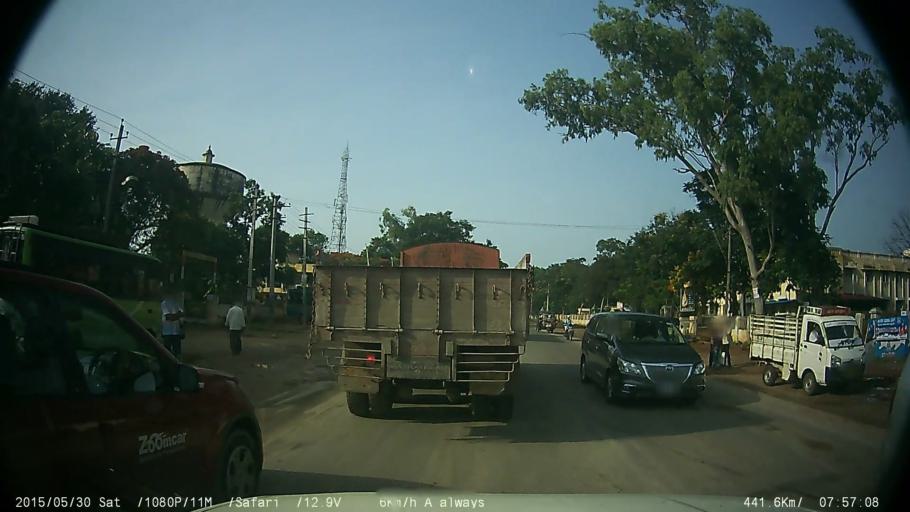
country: IN
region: Karnataka
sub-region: Chamrajnagar
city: Gundlupet
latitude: 11.8093
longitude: 76.6881
